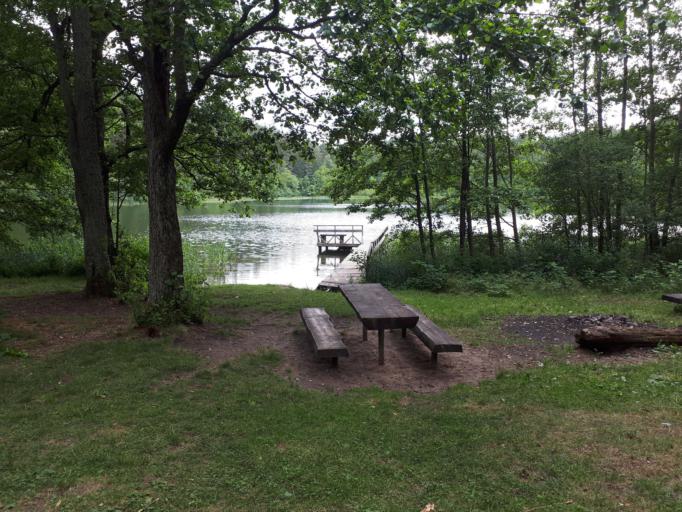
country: LT
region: Alytaus apskritis
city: Druskininkai
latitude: 54.1444
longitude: 24.1075
